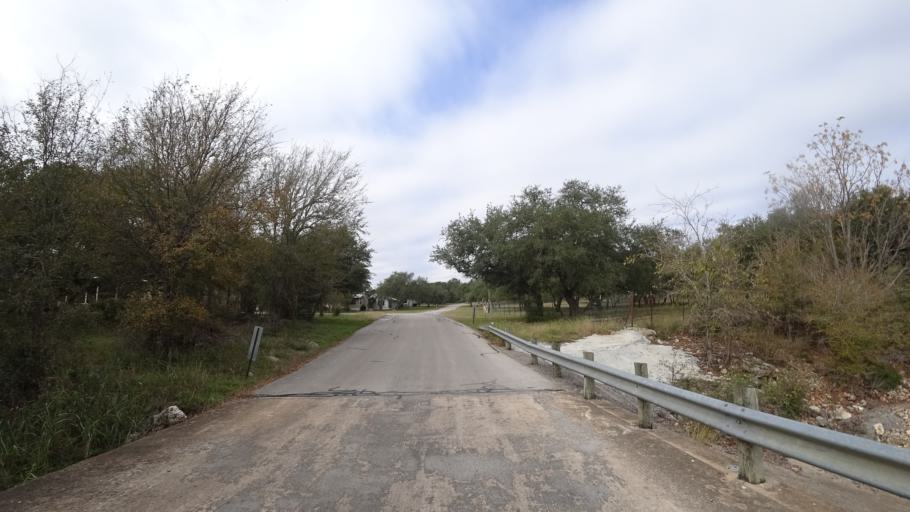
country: US
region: Texas
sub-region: Travis County
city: Shady Hollow
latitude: 30.1375
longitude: -97.8944
